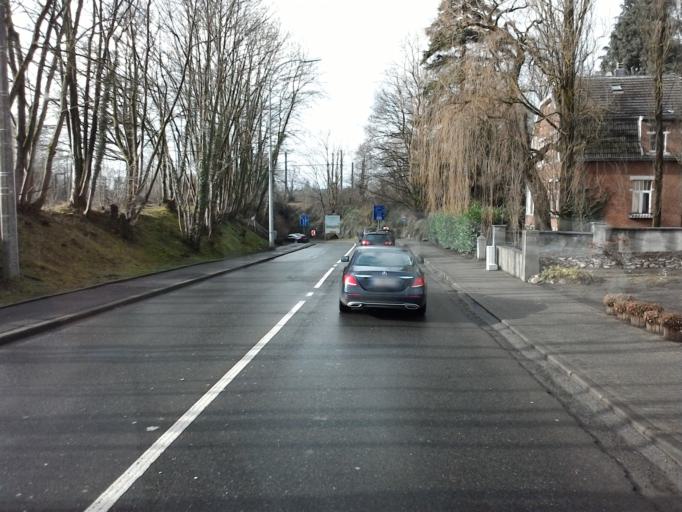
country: BE
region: Wallonia
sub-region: Province de Liege
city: Eupen
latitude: 50.6357
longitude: 6.0372
